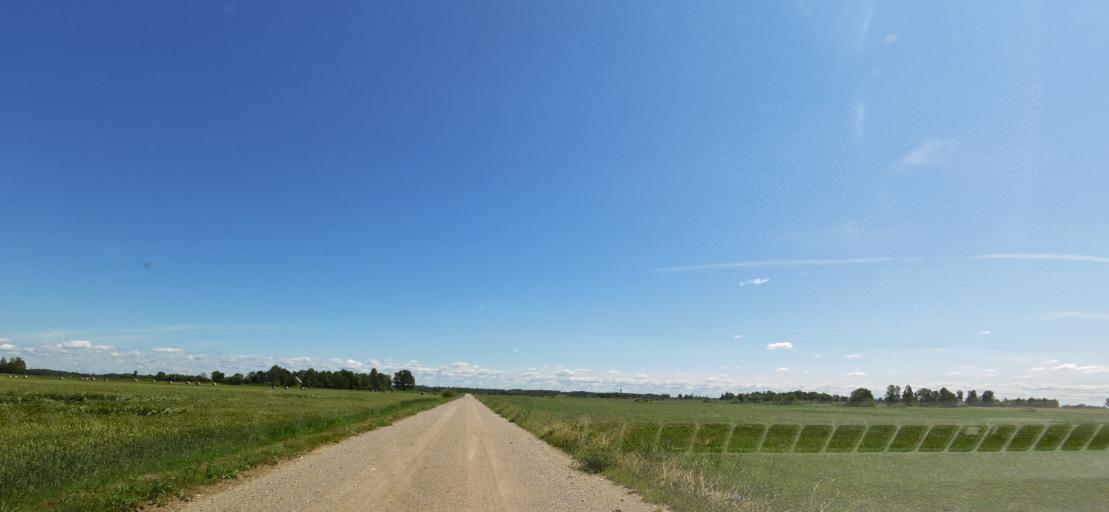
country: LT
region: Panevezys
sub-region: Birzai
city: Birzai
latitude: 56.2604
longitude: 24.5256
